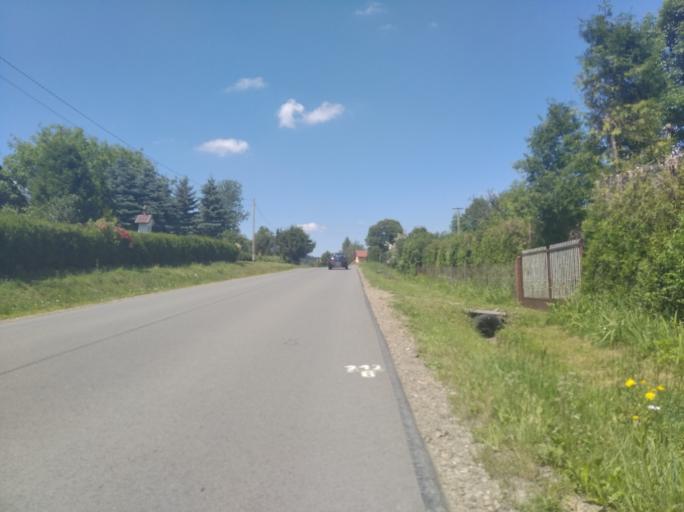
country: PL
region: Subcarpathian Voivodeship
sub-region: Powiat brzozowski
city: Jablonka
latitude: 49.6976
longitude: 22.1350
